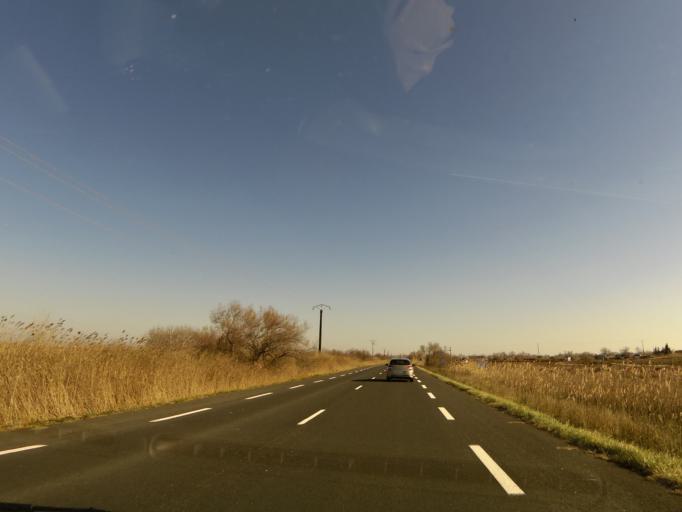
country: FR
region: Languedoc-Roussillon
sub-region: Departement du Gard
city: Aigues-Mortes
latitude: 43.5541
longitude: 4.3270
